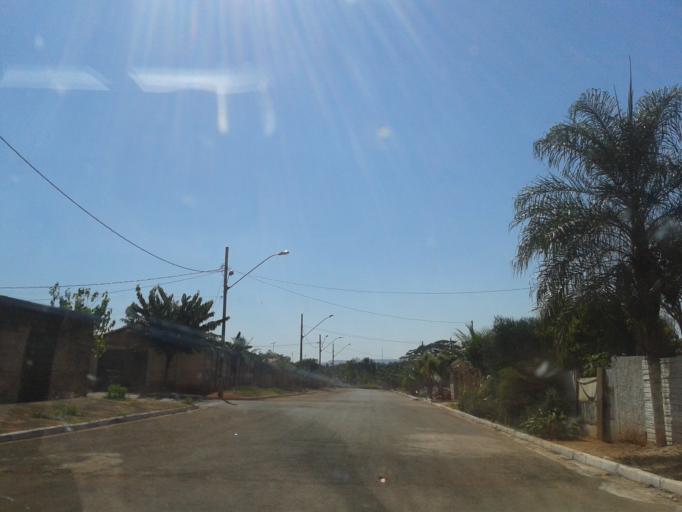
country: BR
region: Minas Gerais
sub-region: Ituiutaba
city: Ituiutaba
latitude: -19.0079
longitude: -49.4793
